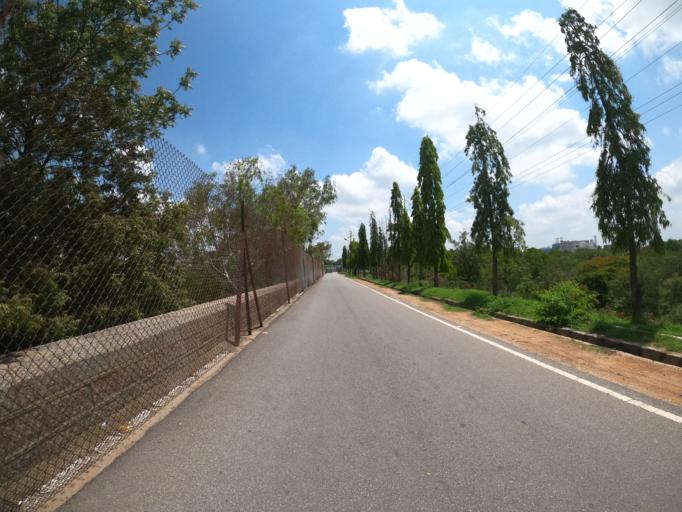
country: IN
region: Telangana
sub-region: Medak
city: Serilingampalle
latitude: 17.3850
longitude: 78.3166
